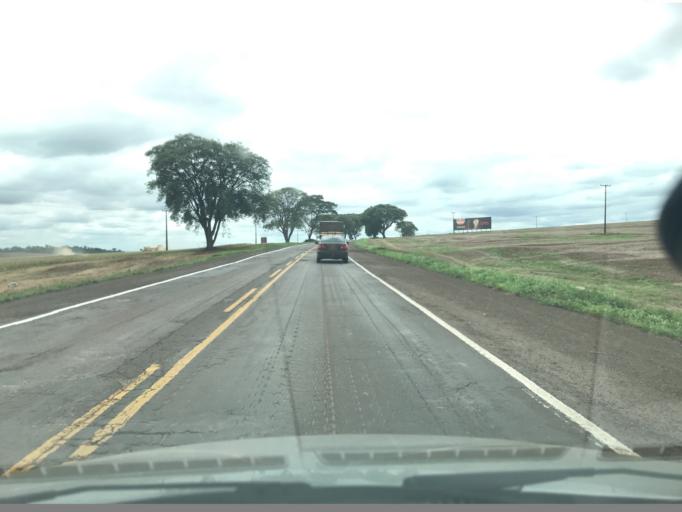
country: BR
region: Parana
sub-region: Terra Boa
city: Terra Boa
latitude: -23.6066
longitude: -52.4161
